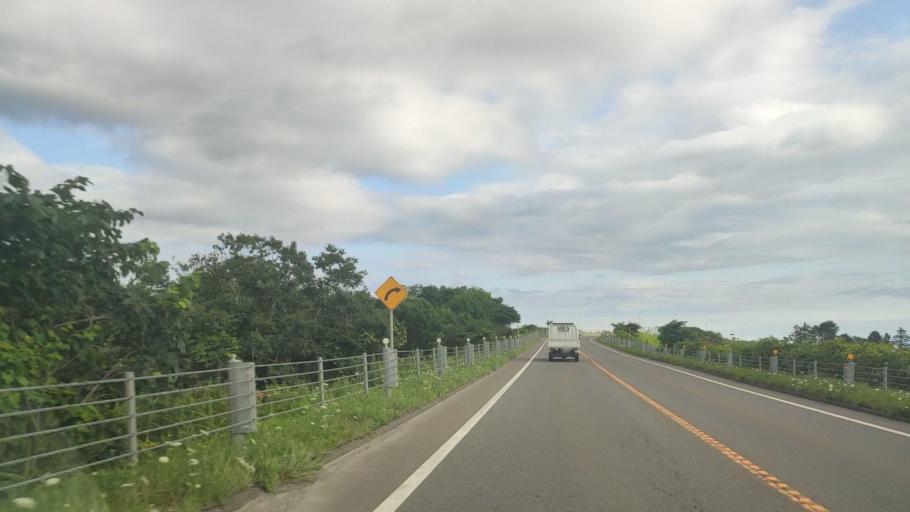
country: JP
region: Hokkaido
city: Niseko Town
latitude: 42.5822
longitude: 140.4533
